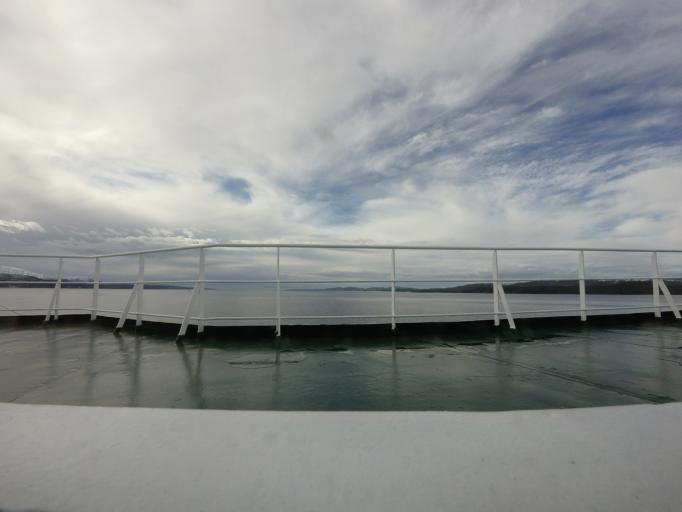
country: NO
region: Sor-Trondelag
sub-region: Hitra
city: Fillan
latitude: 63.4688
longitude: 8.9136
